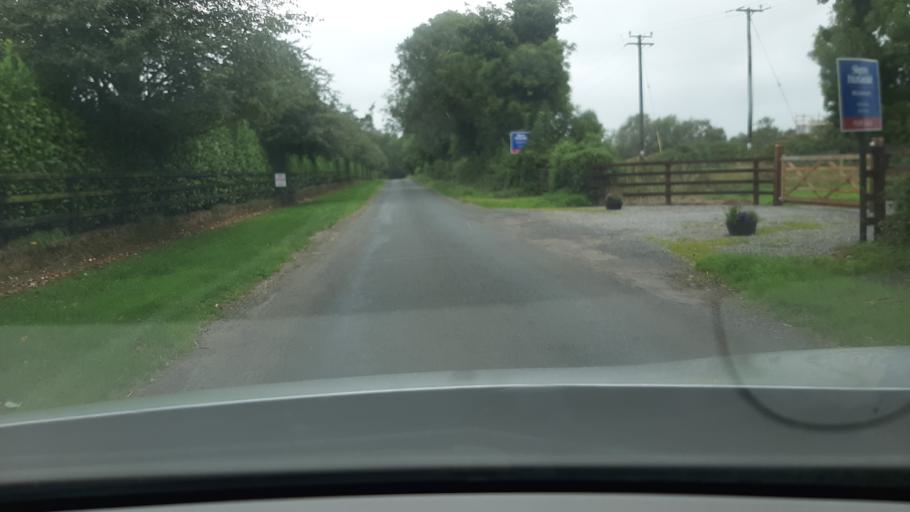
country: IE
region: Leinster
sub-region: Kildare
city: Rathangan
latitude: 53.2064
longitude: -7.0022
